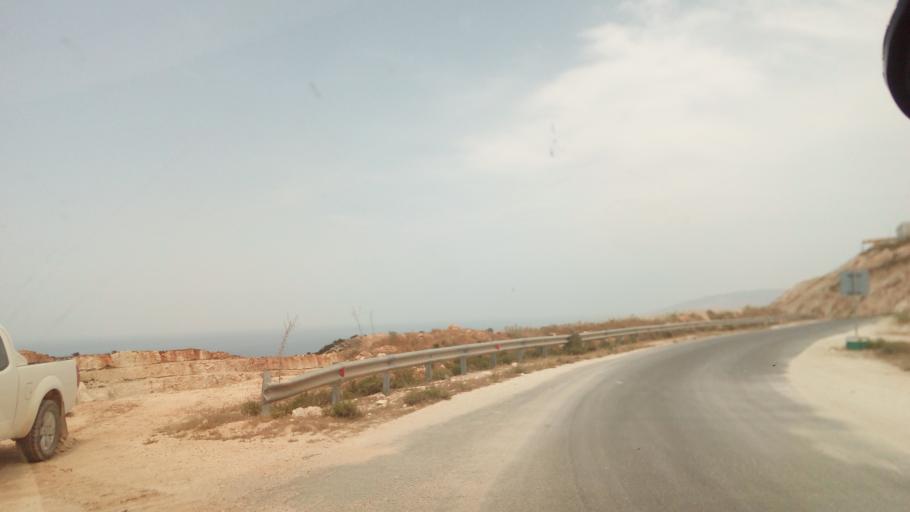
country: CY
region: Pafos
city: Polis
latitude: 35.0027
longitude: 32.3861
